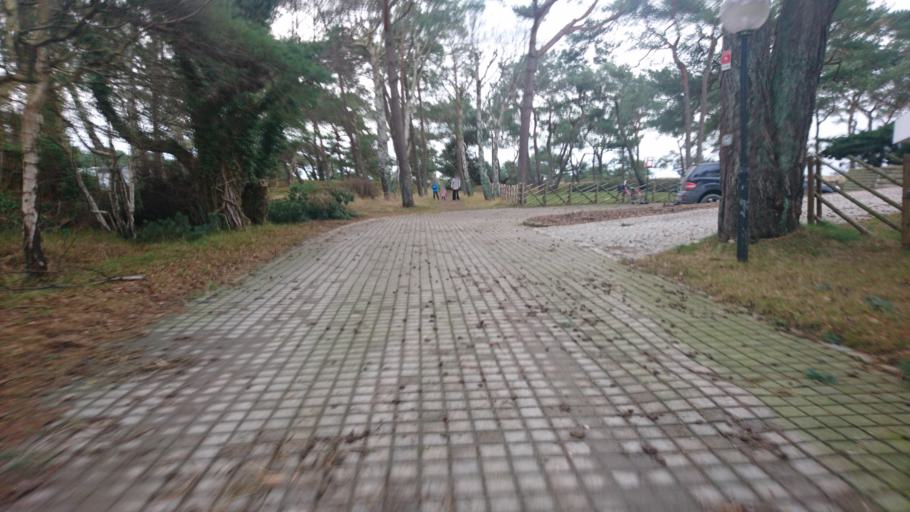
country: SE
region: Skane
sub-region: Vellinge Kommun
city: Ljunghusen
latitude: 55.3885
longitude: 12.9178
